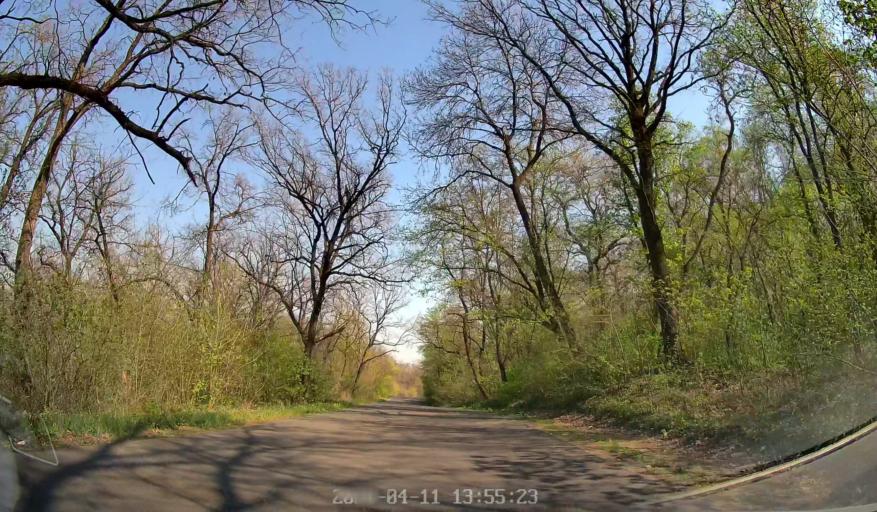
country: MD
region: Chisinau
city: Vadul lui Voda
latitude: 47.0718
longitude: 29.1128
